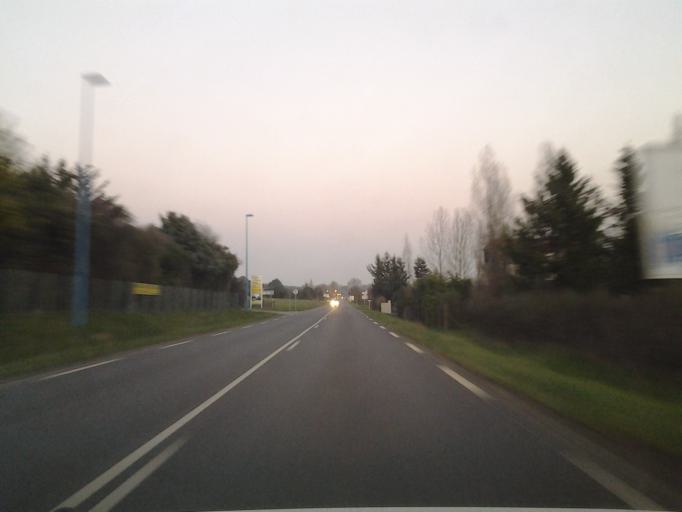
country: FR
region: Pays de la Loire
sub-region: Departement de la Vendee
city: Saint-Gervais
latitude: 46.9052
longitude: -2.0214
